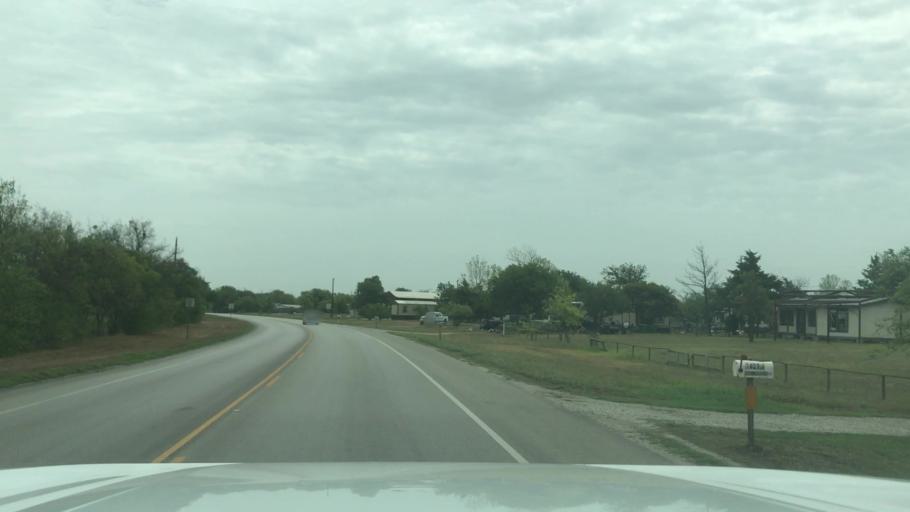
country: US
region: Texas
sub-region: Erath County
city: Dublin
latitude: 32.0892
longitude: -98.3583
